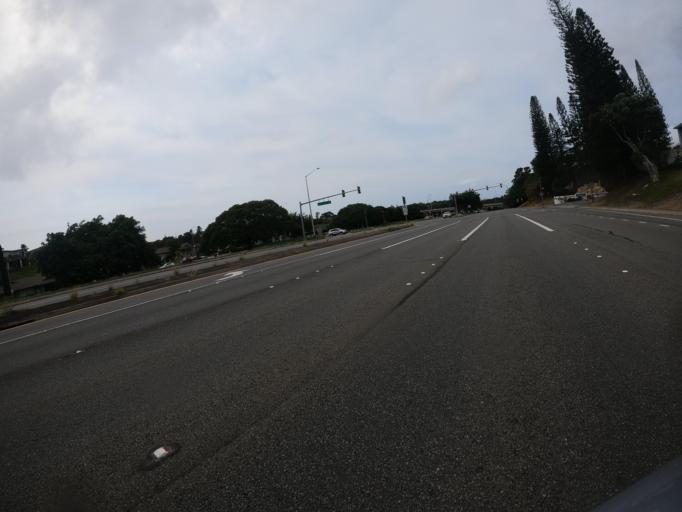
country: US
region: Hawaii
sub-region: Honolulu County
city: Halawa
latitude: 21.3678
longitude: -157.9249
